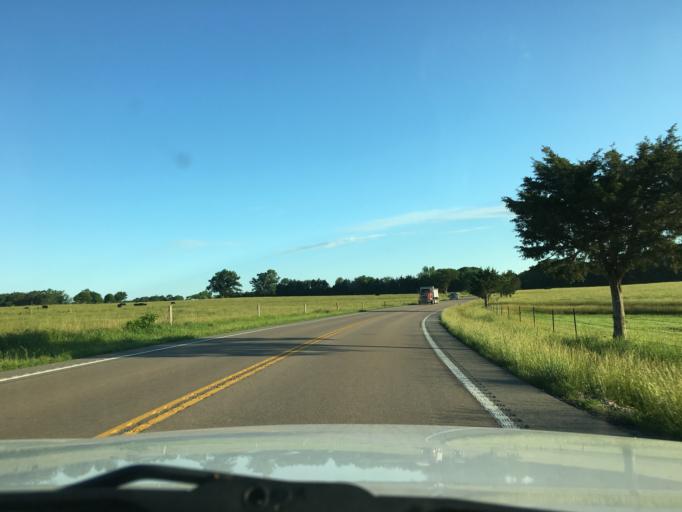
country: US
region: Missouri
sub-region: Gasconade County
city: Owensville
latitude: 38.4403
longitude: -91.4453
